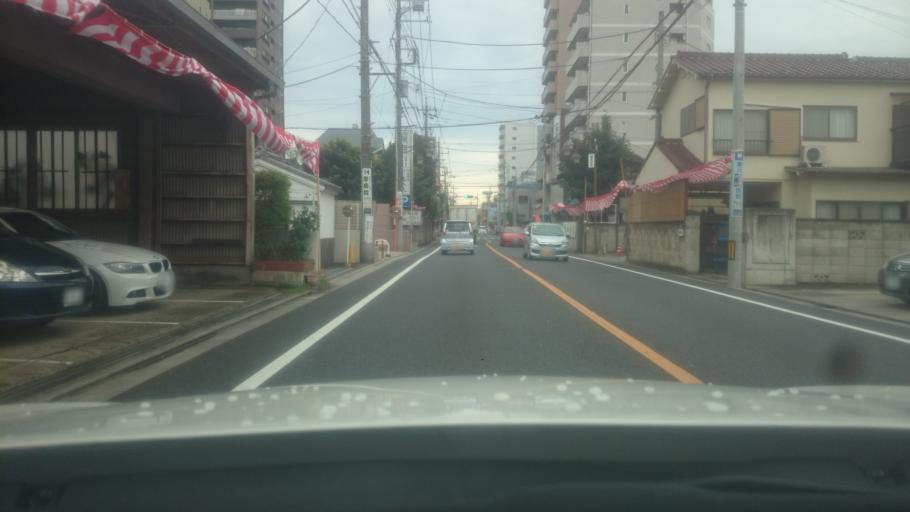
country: JP
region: Saitama
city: Kawagoe
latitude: 35.9064
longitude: 139.4867
